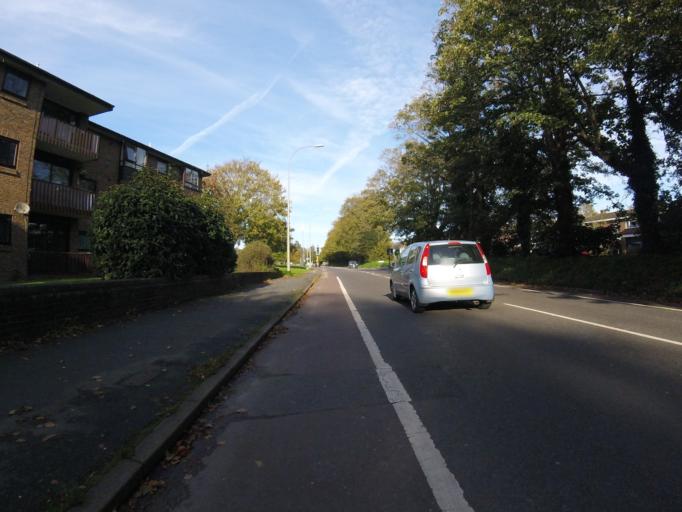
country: GB
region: England
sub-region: Brighton and Hove
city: Hove
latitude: 50.8573
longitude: -0.1533
